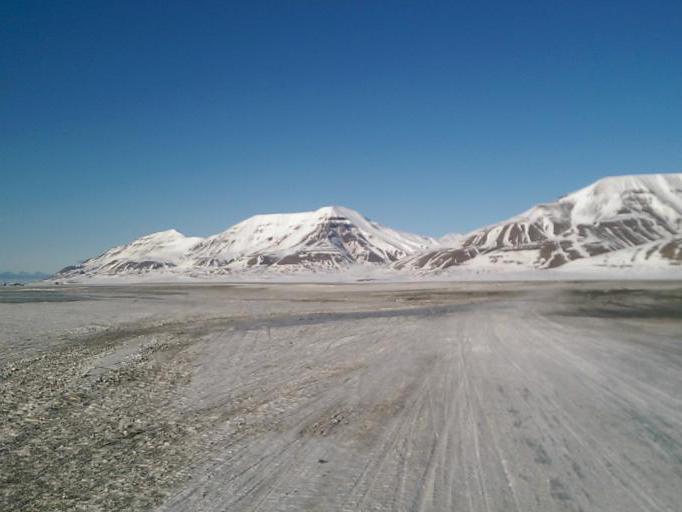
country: SJ
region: Svalbard
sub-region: Spitsbergen
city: Longyearbyen
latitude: 78.1906
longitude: 15.8663
